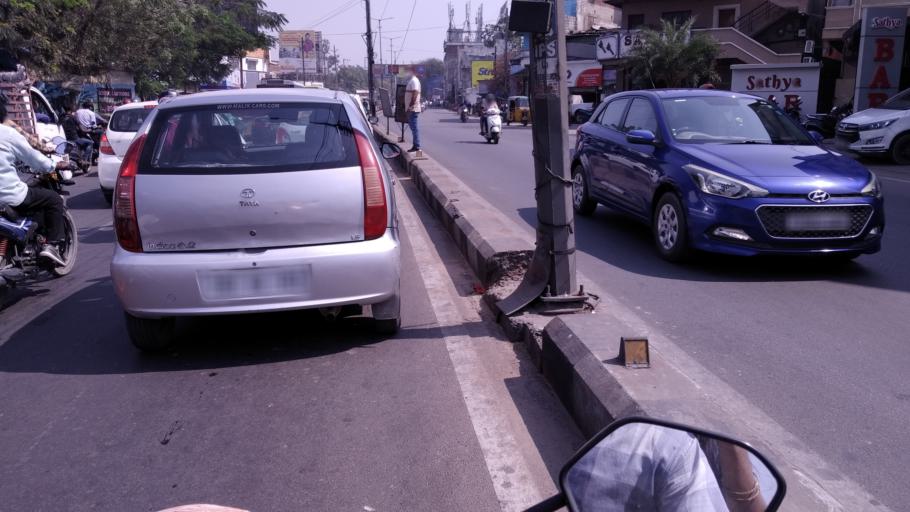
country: IN
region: Telangana
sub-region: Hyderabad
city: Malkajgiri
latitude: 17.4560
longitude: 78.4834
